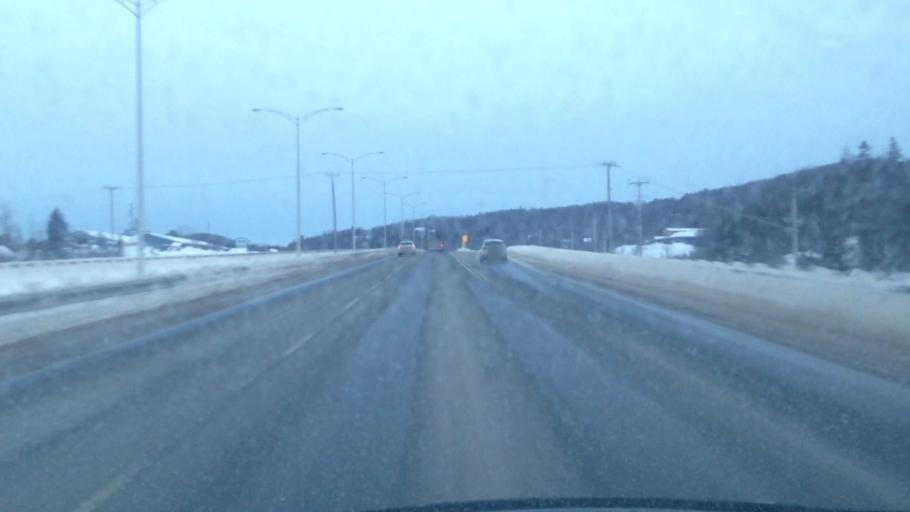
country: CA
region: Quebec
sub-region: Laurentides
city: Mont-Tremblant
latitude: 46.1097
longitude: -74.4894
